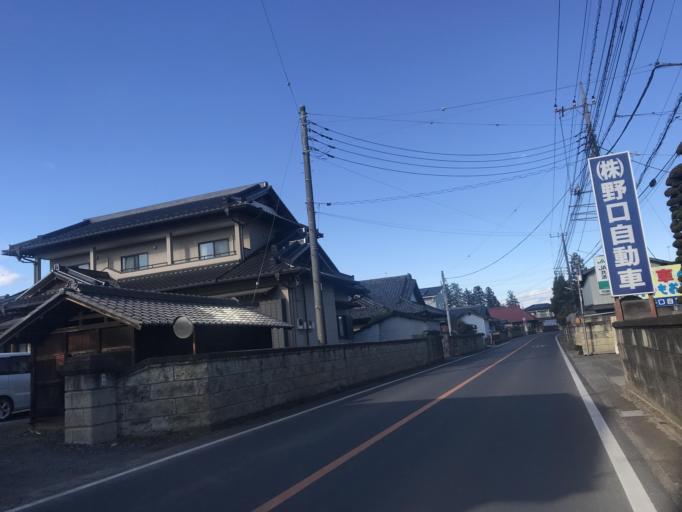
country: JP
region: Tochigi
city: Kaminokawa
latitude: 36.4029
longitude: 139.8771
